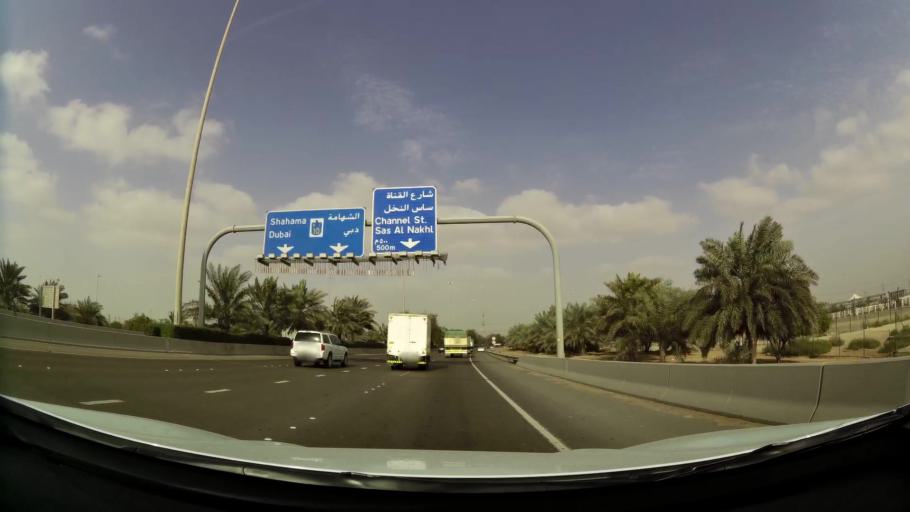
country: AE
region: Abu Dhabi
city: Abu Dhabi
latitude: 24.4182
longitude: 54.5084
